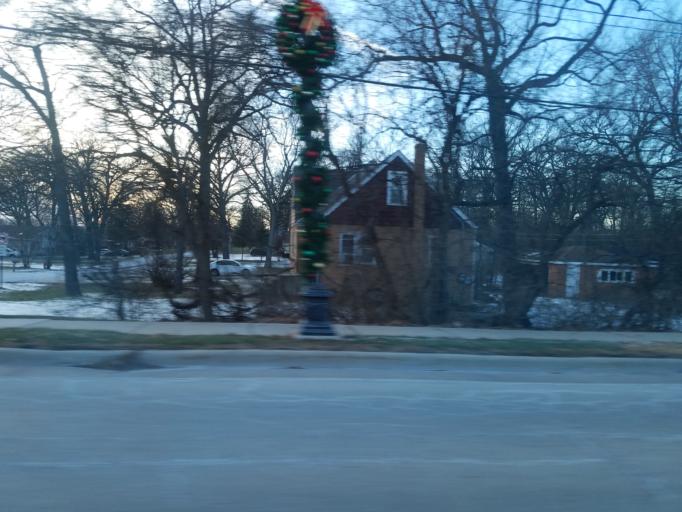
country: US
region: Illinois
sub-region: DuPage County
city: Wood Dale
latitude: 41.9697
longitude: -87.9789
